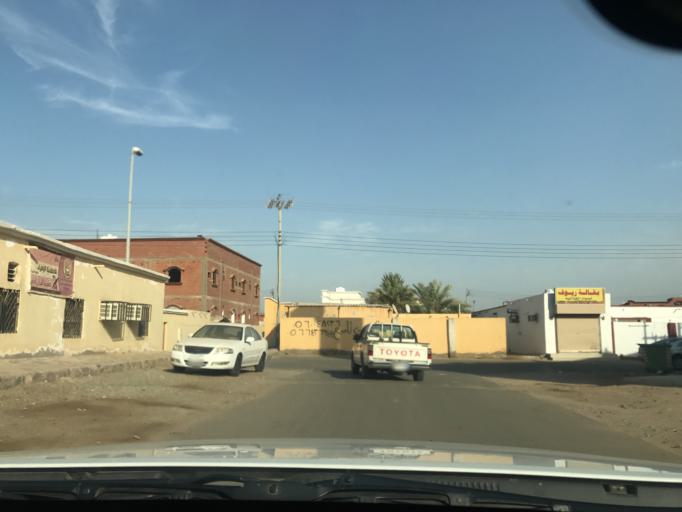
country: SA
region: Makkah
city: Al Jumum
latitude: 21.4404
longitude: 39.5223
